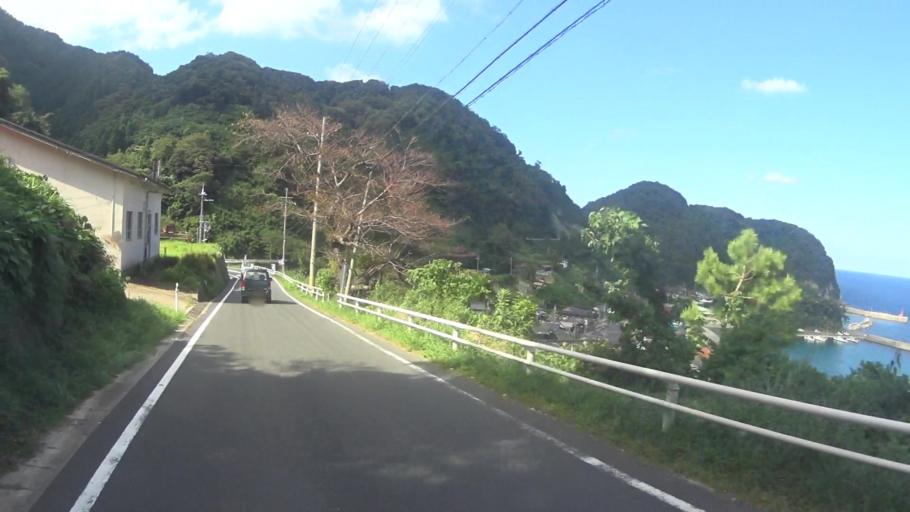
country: JP
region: Kyoto
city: Miyazu
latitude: 35.7502
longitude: 135.2509
